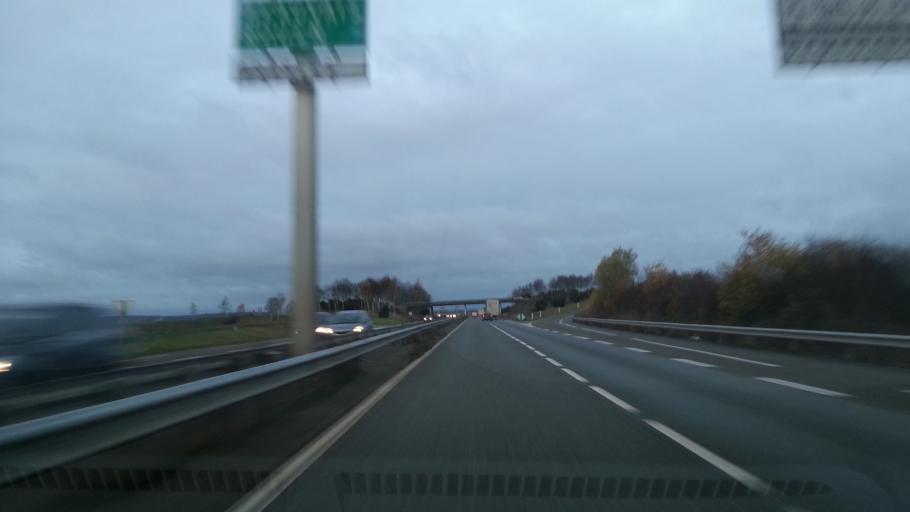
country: FR
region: Picardie
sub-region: Departement de l'Oise
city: Bresles
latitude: 49.4141
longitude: 2.3069
